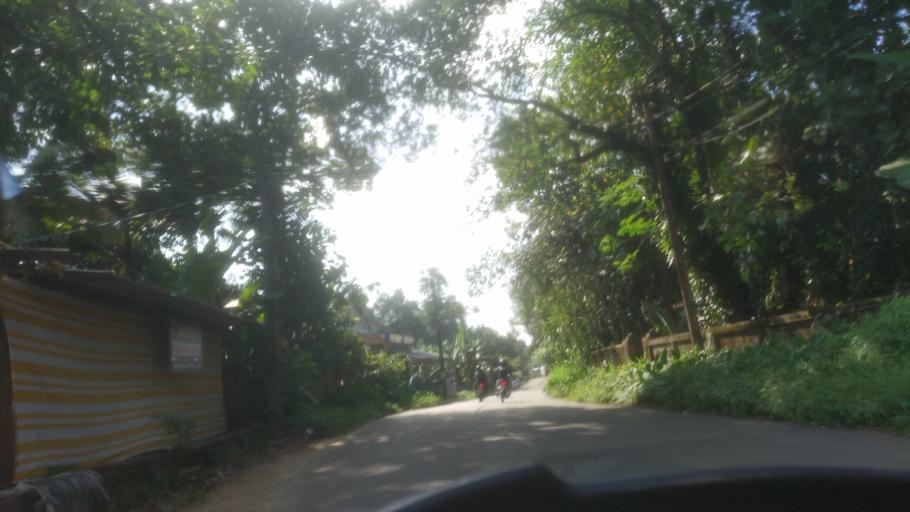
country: IN
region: Kerala
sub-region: Ernakulam
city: Muvattupula
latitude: 9.9980
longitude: 76.6222
